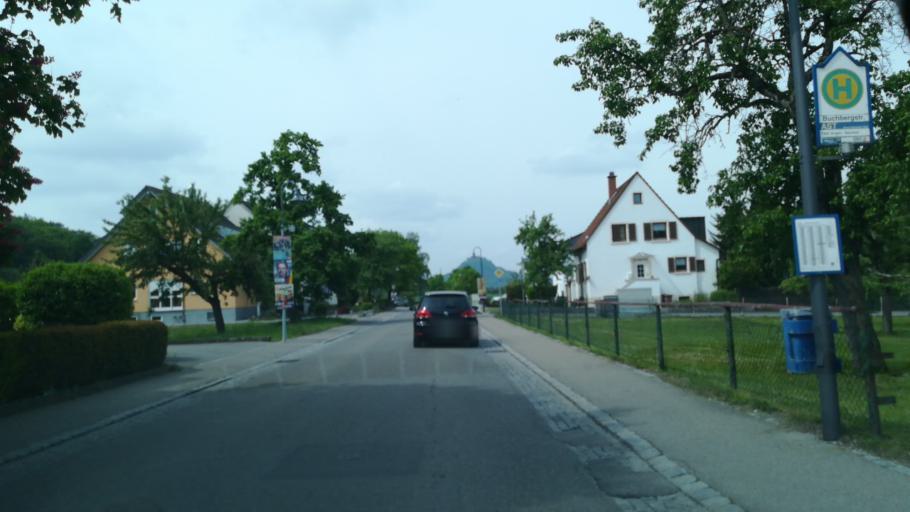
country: DE
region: Baden-Wuerttemberg
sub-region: Freiburg Region
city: Volkertshausen
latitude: 47.7833
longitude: 8.8735
